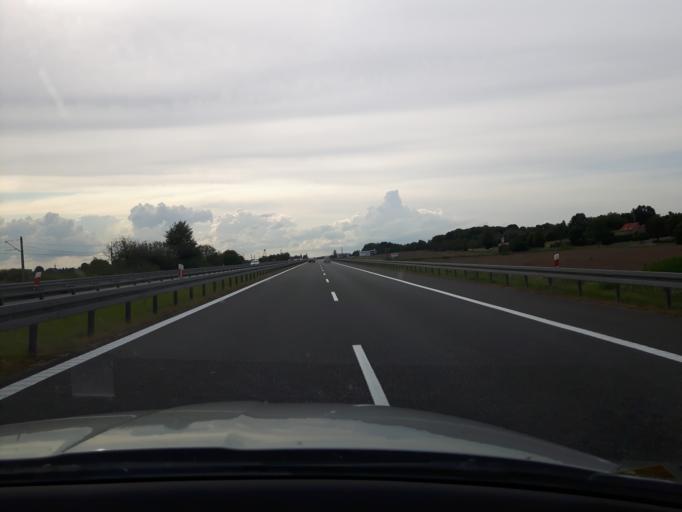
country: PL
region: Warmian-Masurian Voivodeship
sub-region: Powiat elblaski
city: Gronowo Gorne
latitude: 54.1062
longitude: 19.5053
